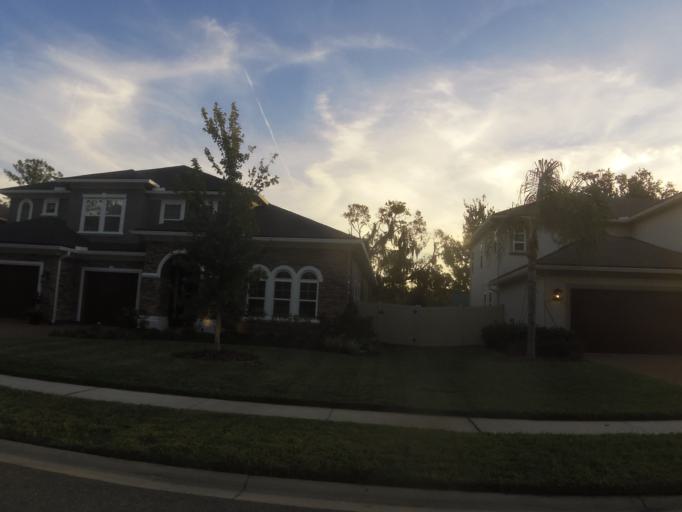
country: US
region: Florida
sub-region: Saint Johns County
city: Palm Valley
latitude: 30.1811
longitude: -81.3886
